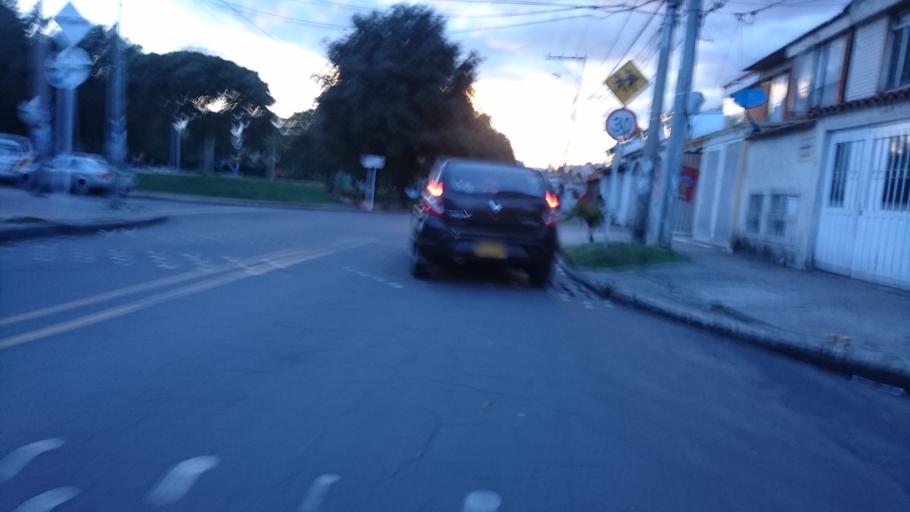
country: CO
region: Bogota D.C.
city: Barrio San Luis
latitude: 4.6856
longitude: -74.0662
